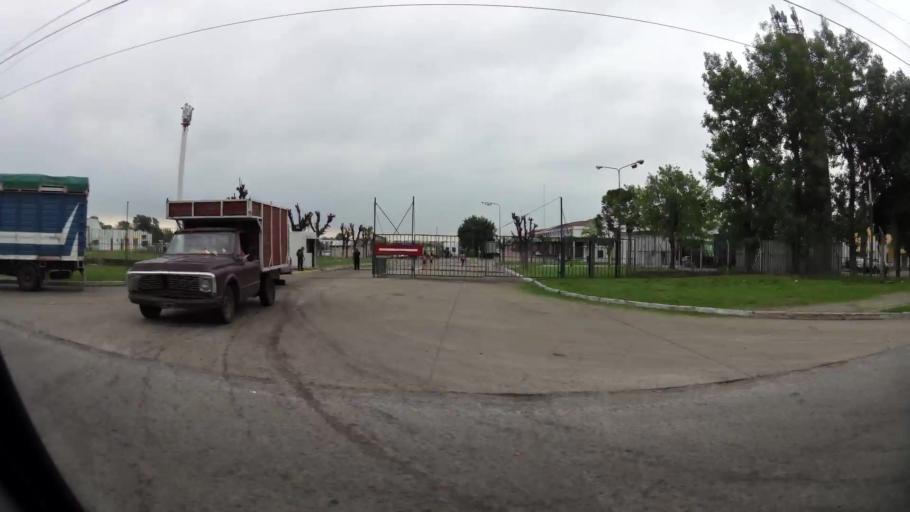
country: AR
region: Buenos Aires
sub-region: Partido de La Plata
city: La Plata
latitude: -34.8833
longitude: -57.9749
